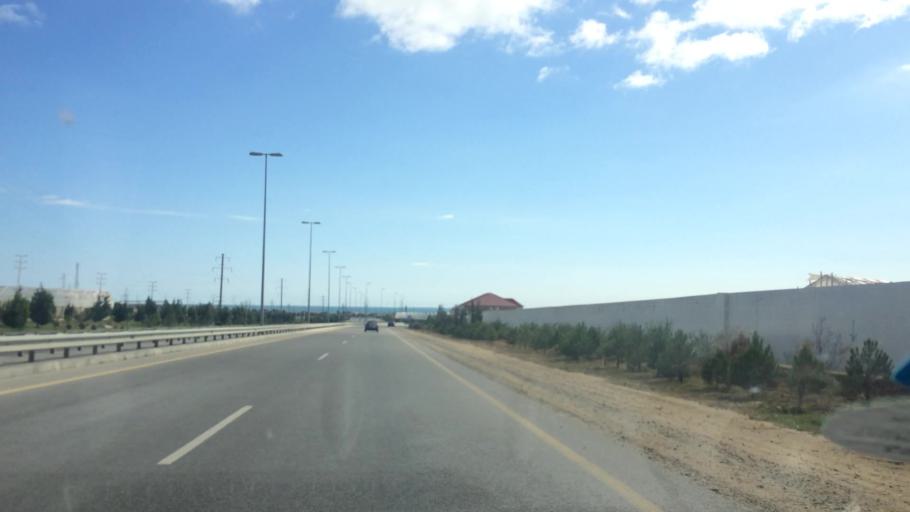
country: AZ
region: Baki
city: Zyrya
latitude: 40.3999
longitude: 50.3164
